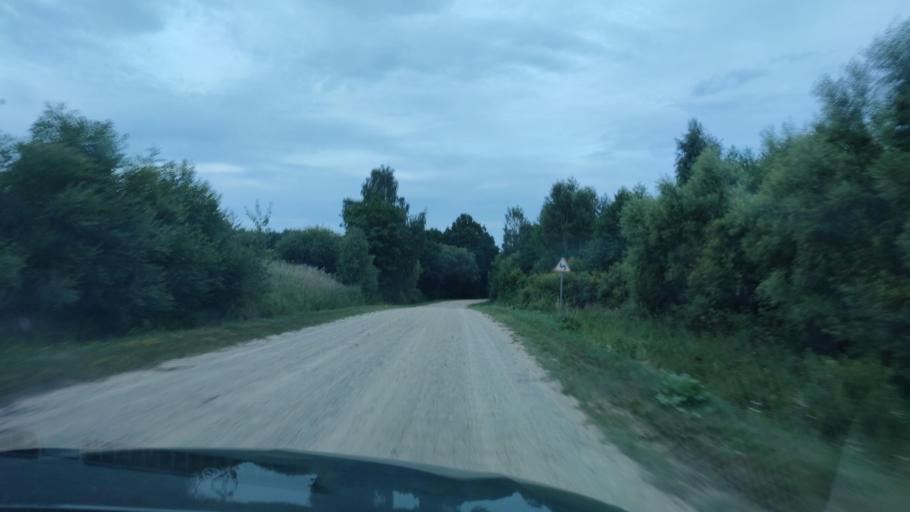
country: BY
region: Vitebsk
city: Mosar
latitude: 55.0736
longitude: 27.2065
